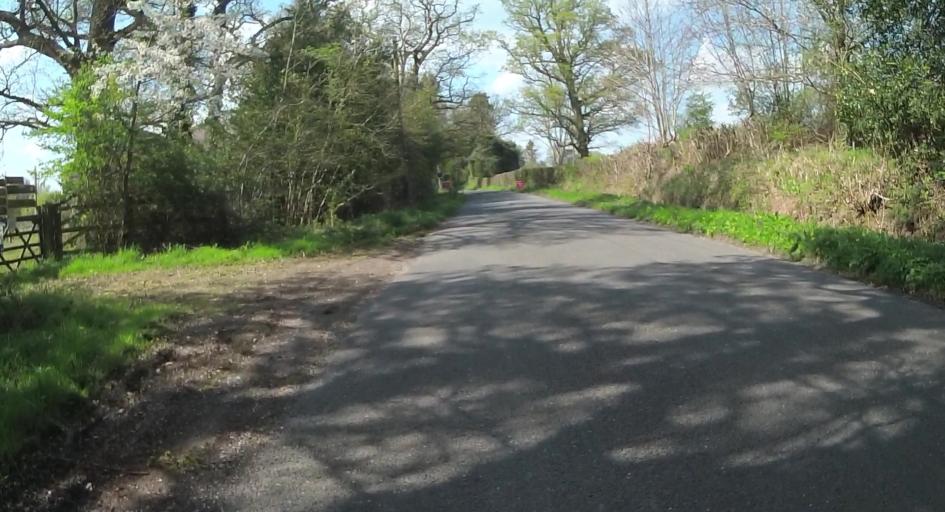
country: GB
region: England
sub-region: Hampshire
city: Tadley
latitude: 51.3509
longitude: -1.0947
